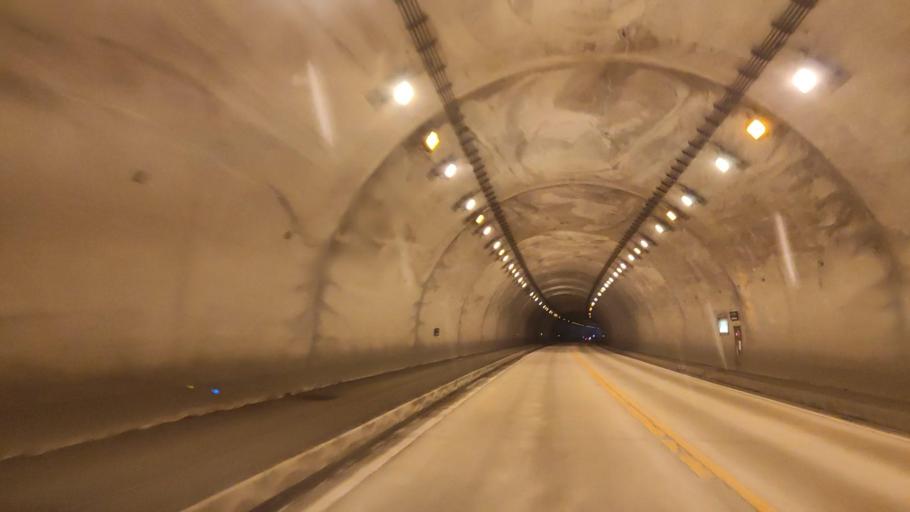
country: JP
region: Hyogo
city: Toyooka
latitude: 35.4598
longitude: 134.7685
